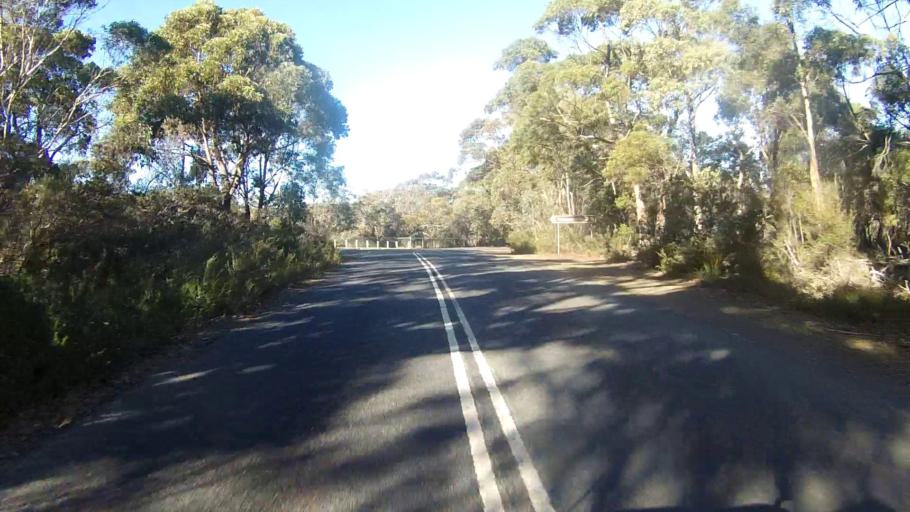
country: AU
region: Tasmania
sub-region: Clarence
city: Sandford
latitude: -43.0417
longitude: 147.9499
